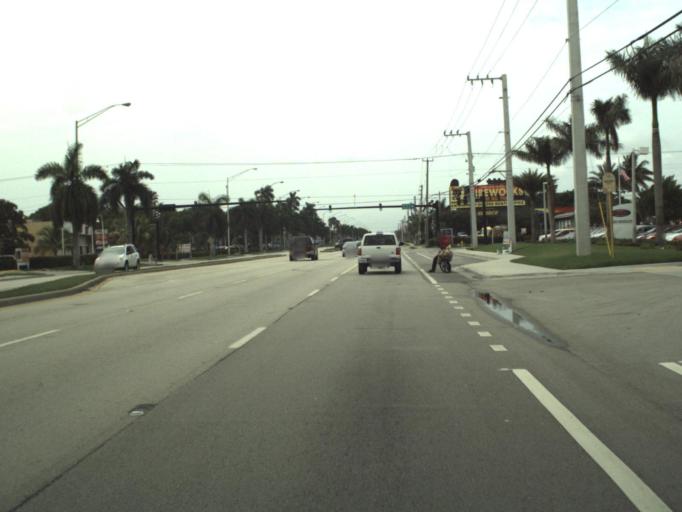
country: US
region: Florida
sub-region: Broward County
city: Hillsboro Beach
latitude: 26.2988
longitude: -80.0940
